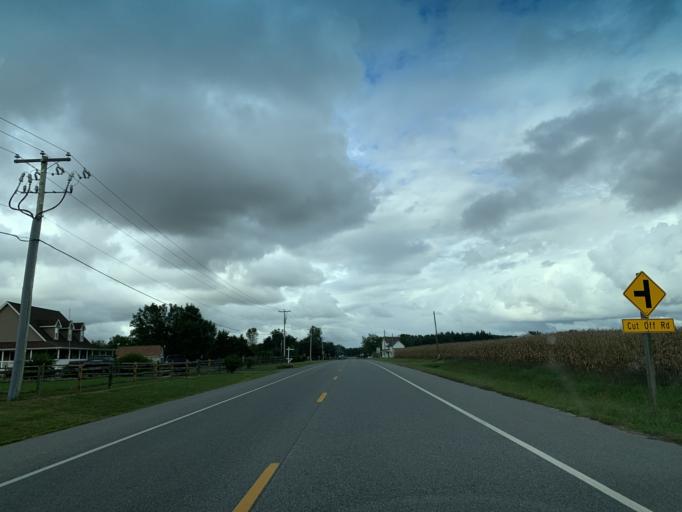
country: US
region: Maryland
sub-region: Caroline County
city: Ridgely
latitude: 39.0281
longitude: -75.8754
